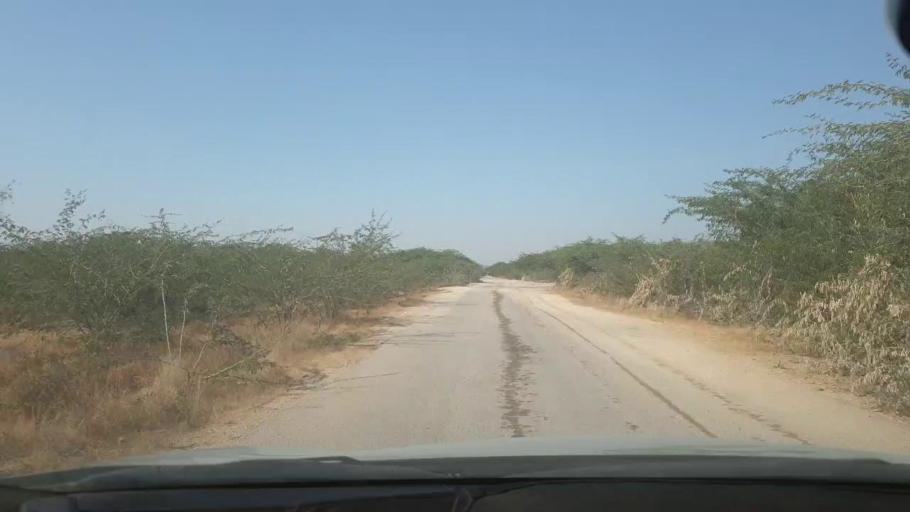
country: PK
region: Sindh
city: Malir Cantonment
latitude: 25.1481
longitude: 67.1654
